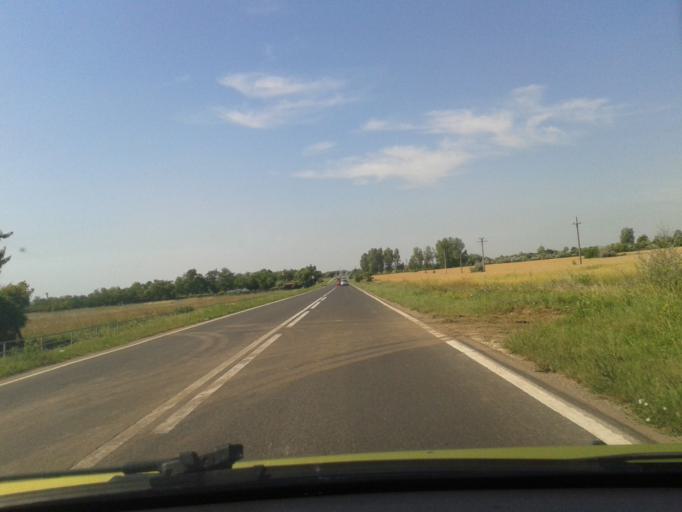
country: RO
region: Constanta
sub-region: Municipiul Mangalia
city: Mangalia
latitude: 43.7761
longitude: 28.5778
